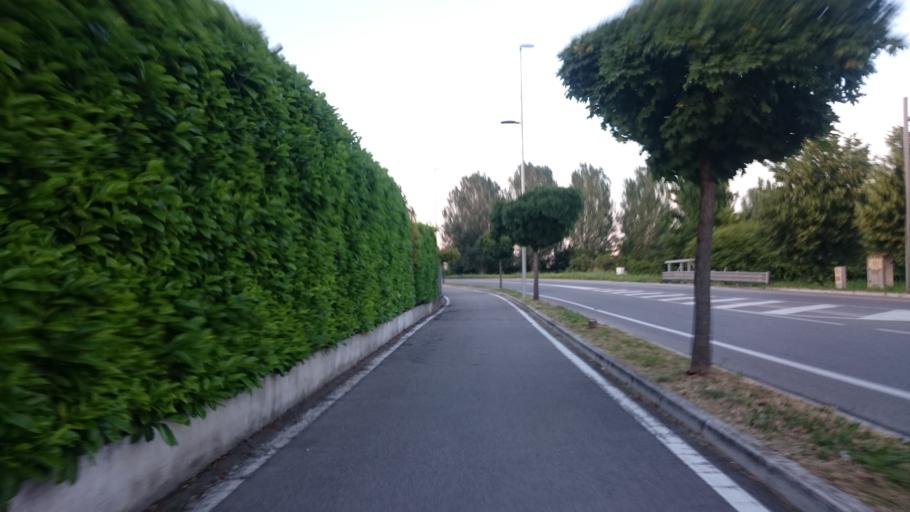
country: IT
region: Veneto
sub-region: Provincia di Verona
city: Legnago
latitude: 45.1869
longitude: 11.2819
